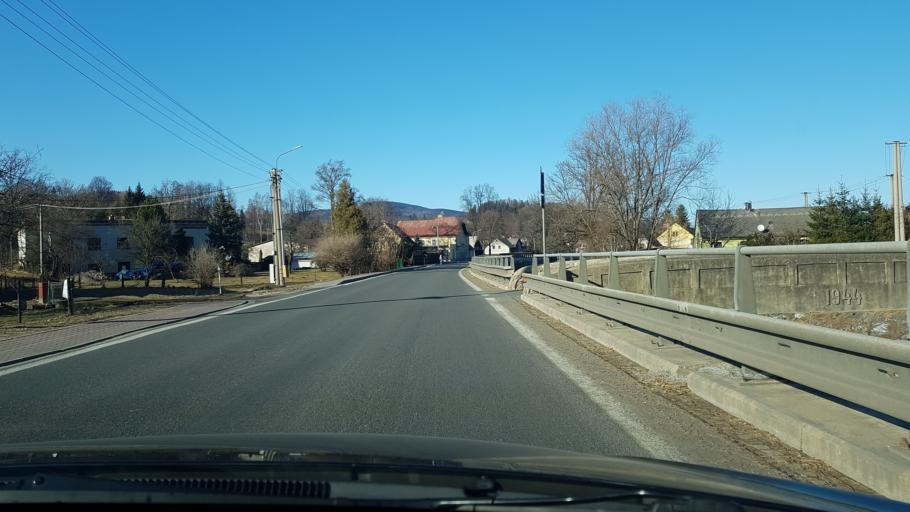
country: CZ
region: Olomoucky
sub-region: Okres Jesenik
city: Jesenik
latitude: 50.1953
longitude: 17.1936
